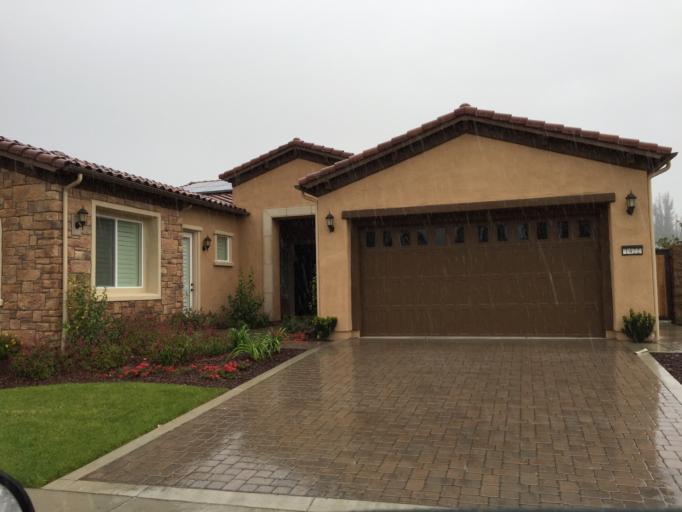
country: US
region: California
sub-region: San Luis Obispo County
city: Callender
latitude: 35.0326
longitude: -120.5436
